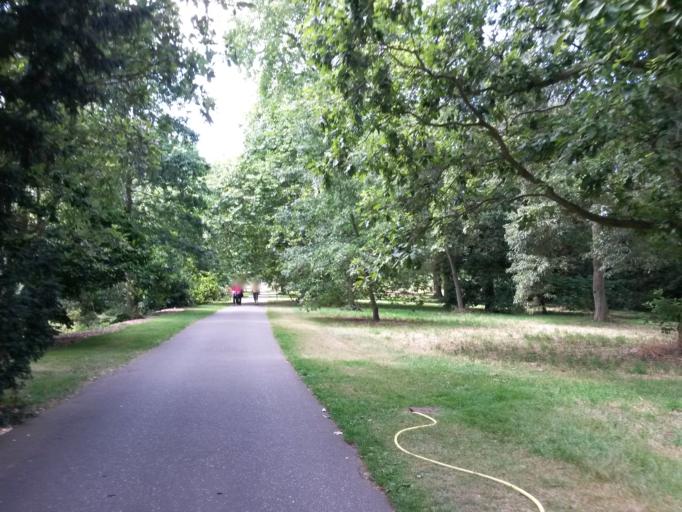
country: GB
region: England
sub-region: Greater London
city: Brentford
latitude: 51.4795
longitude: -0.3010
